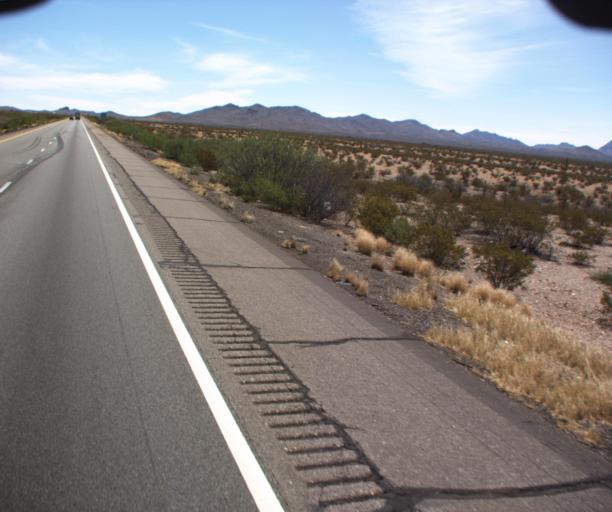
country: US
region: New Mexico
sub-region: Hidalgo County
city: Lordsburg
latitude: 32.2327
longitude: -109.0717
